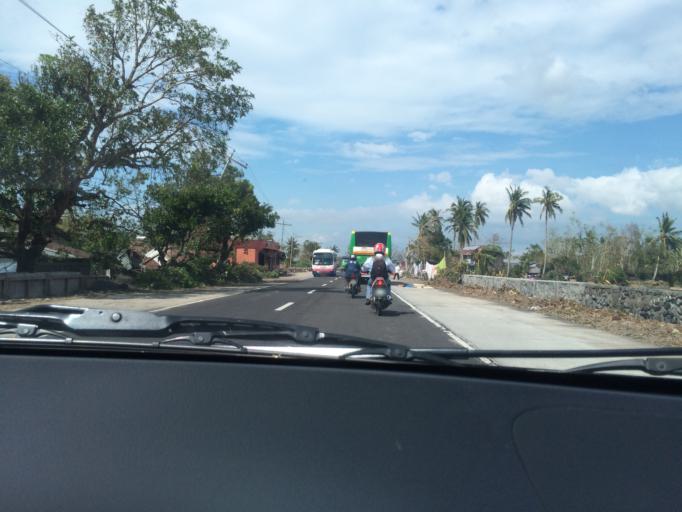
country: PH
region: Bicol
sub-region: Province of Albay
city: Iraya
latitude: 13.2609
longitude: 123.4985
